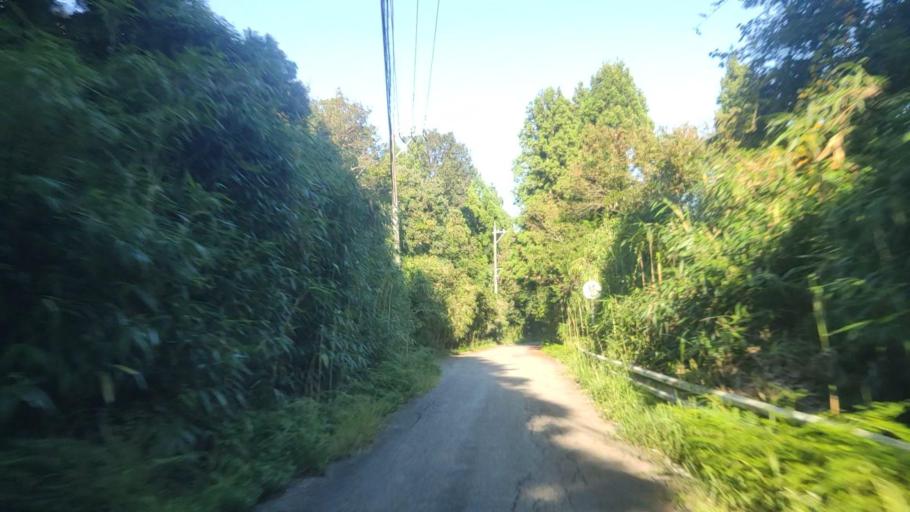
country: JP
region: Ishikawa
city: Nanao
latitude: 37.1342
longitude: 136.9120
